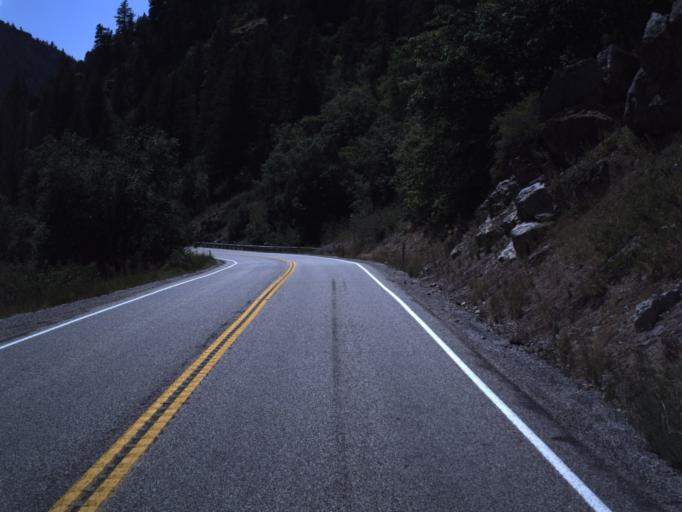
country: US
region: Utah
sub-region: Cache County
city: North Logan
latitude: 41.8070
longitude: -111.6295
